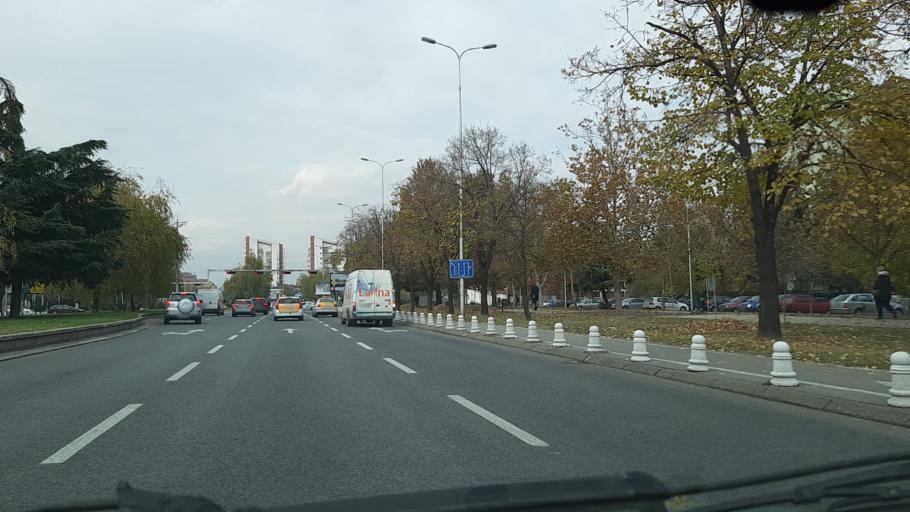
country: MK
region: Kisela Voda
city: Usje
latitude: 41.9873
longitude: 21.4634
